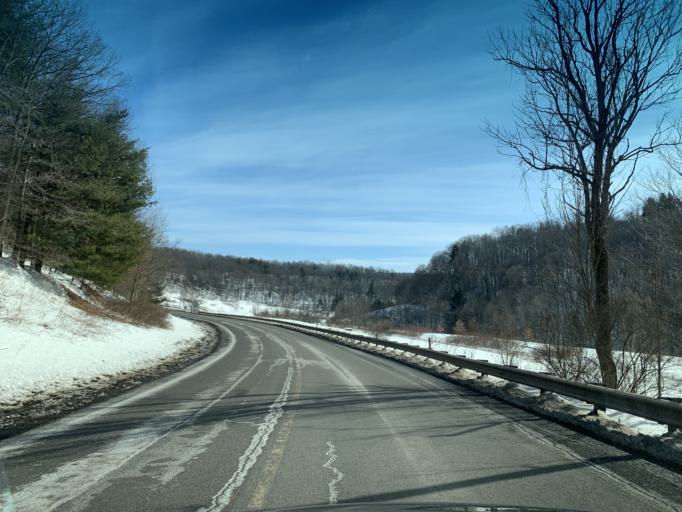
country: US
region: Maryland
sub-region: Allegany County
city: Lonaconing
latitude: 39.5987
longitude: -78.9465
